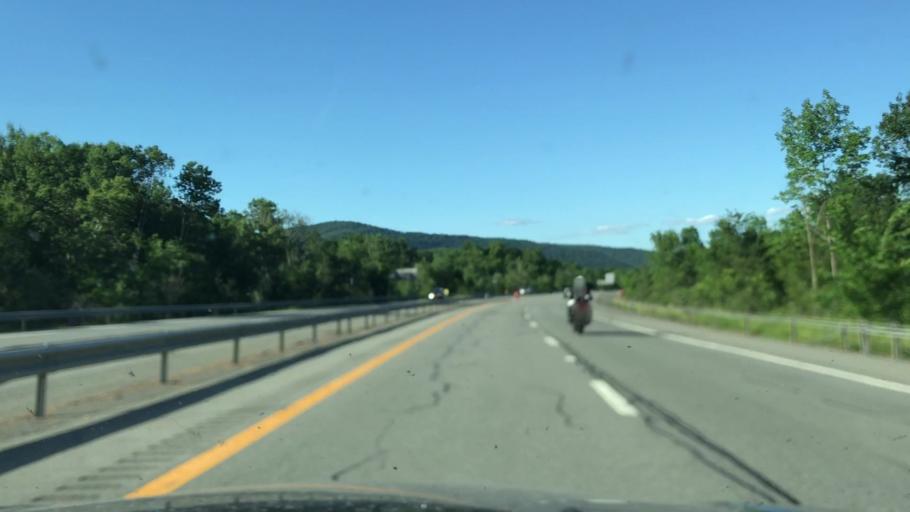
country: US
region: New York
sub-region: Delaware County
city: Hancock
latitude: 41.9748
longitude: -75.1749
